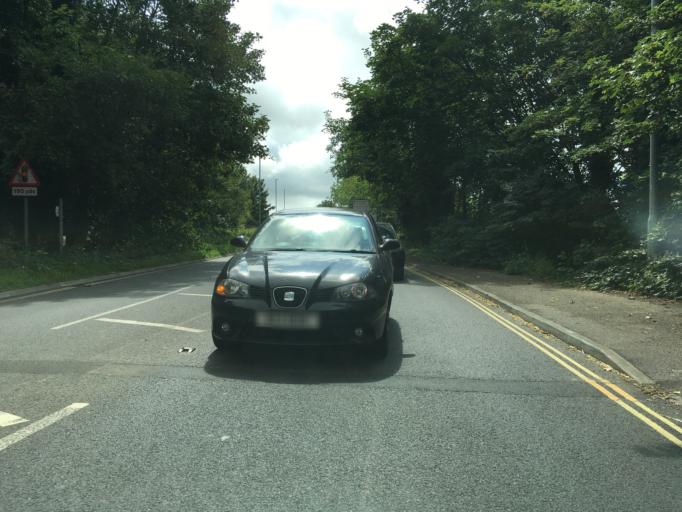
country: GB
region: England
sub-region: Brighton and Hove
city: Rottingdean
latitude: 50.8622
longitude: -0.0799
